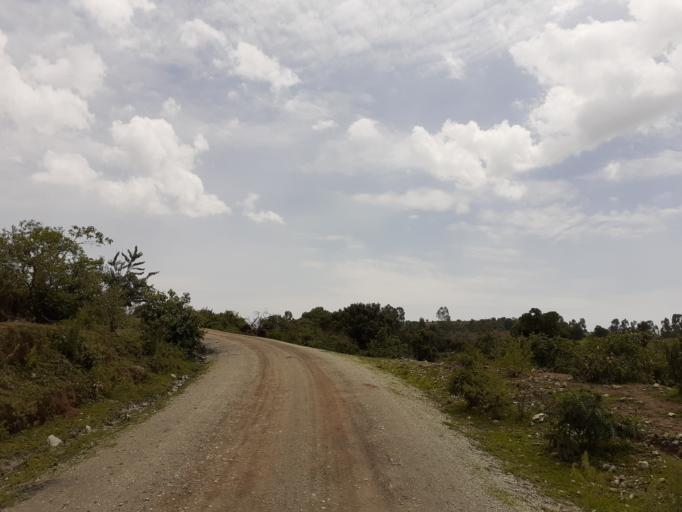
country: ET
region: Oromiya
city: Gimbi
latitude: 9.3367
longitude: 35.7011
